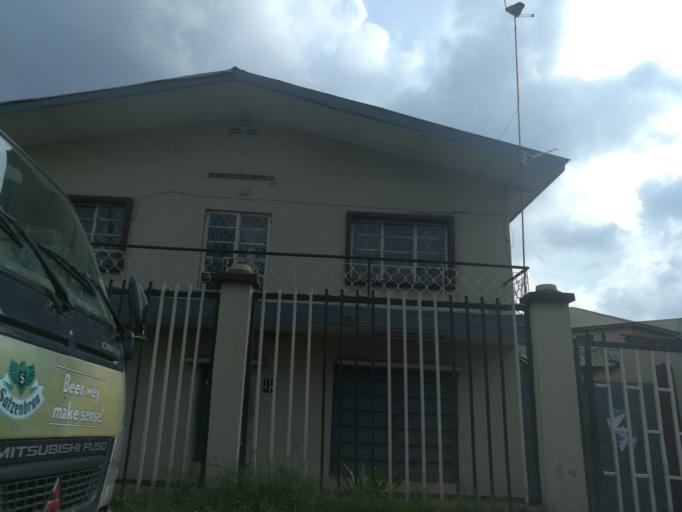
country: NG
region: Lagos
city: Somolu
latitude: 6.5410
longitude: 3.3798
